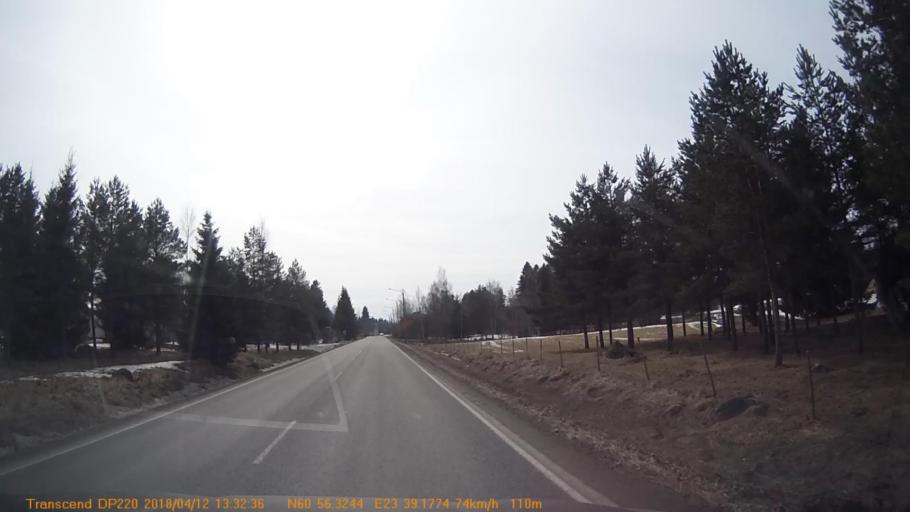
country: FI
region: Haeme
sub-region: Forssa
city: Forssa
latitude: 60.9386
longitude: 23.6528
